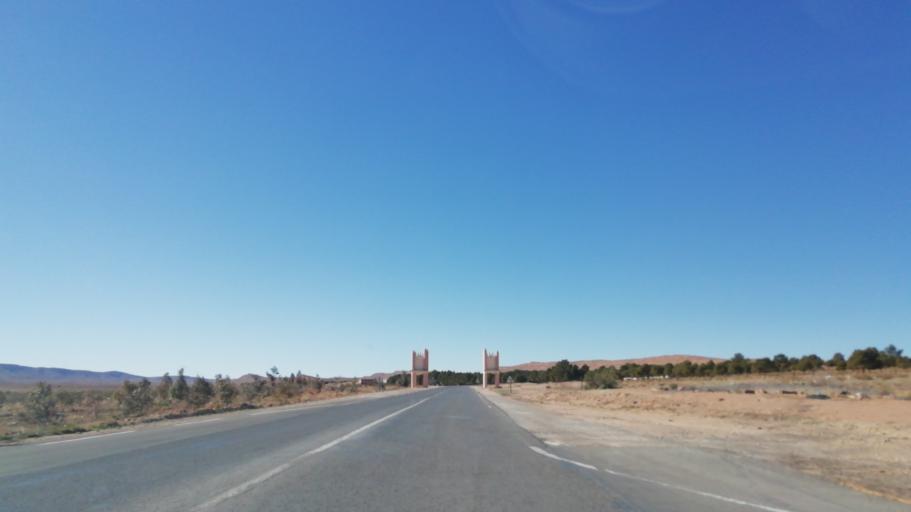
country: DZ
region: El Bayadh
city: El Bayadh
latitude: 33.7228
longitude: 1.5219
